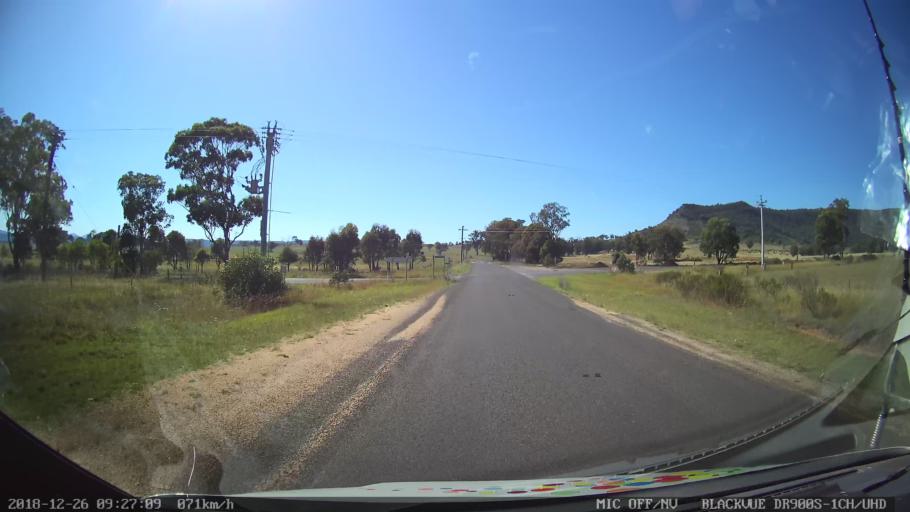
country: AU
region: New South Wales
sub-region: Mid-Western Regional
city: Kandos
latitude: -32.8331
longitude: 150.0150
